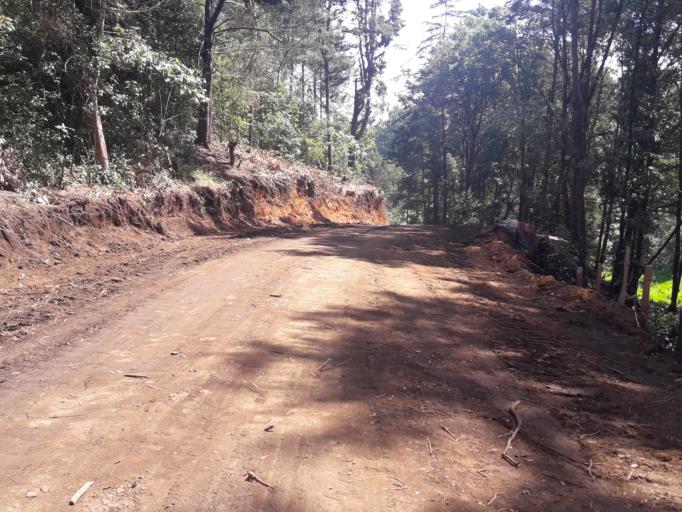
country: GT
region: Quiche
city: Nebaj
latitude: 15.4252
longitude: -91.1371
